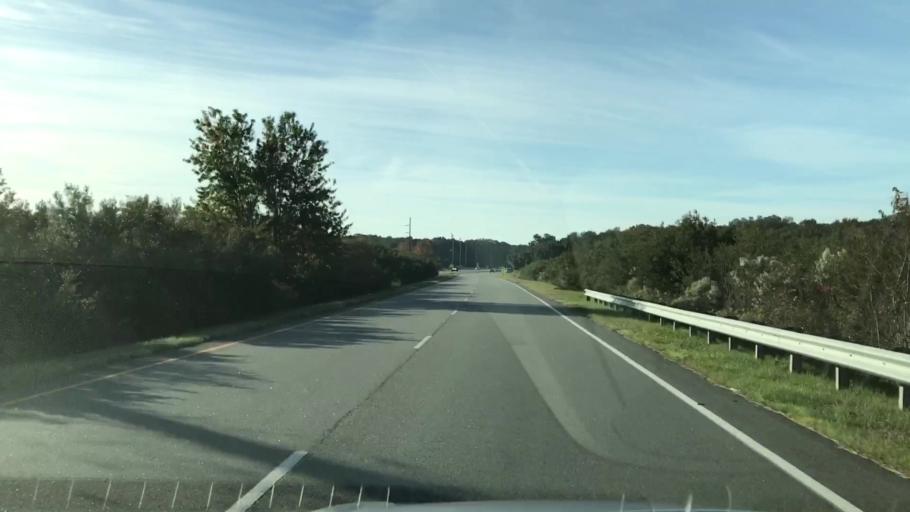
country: US
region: South Carolina
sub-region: Beaufort County
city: Laurel Bay
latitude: 32.5376
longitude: -80.7464
